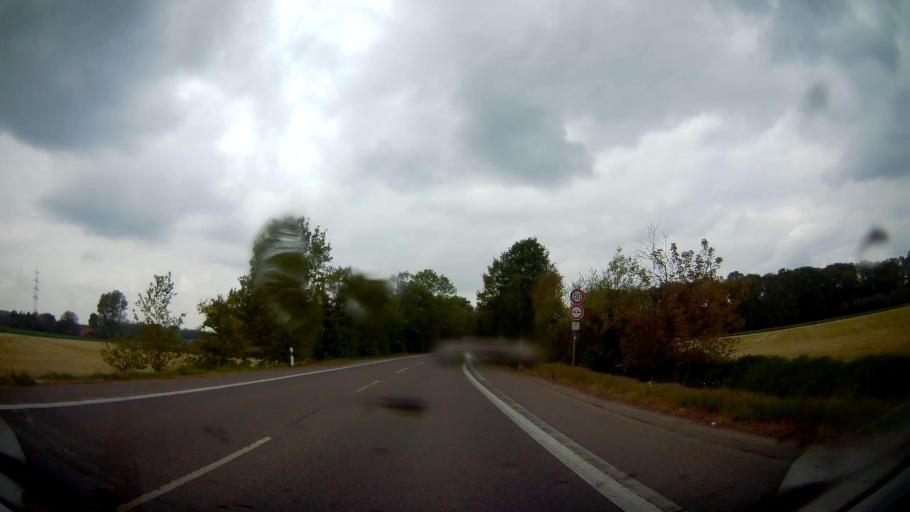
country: DE
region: North Rhine-Westphalia
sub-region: Regierungsbezirk Munster
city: Gladbeck
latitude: 51.5826
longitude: 6.9491
